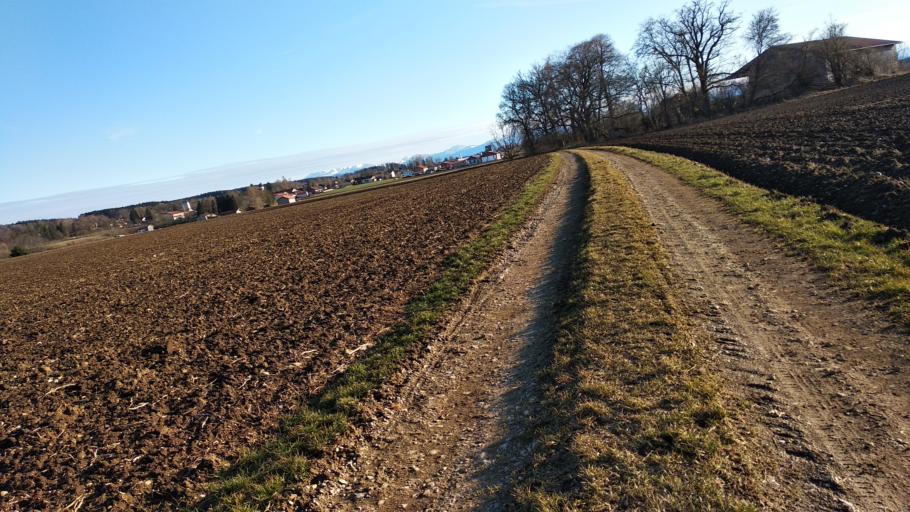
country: DE
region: Bavaria
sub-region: Upper Bavaria
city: Aying
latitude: 47.9818
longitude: 11.7722
